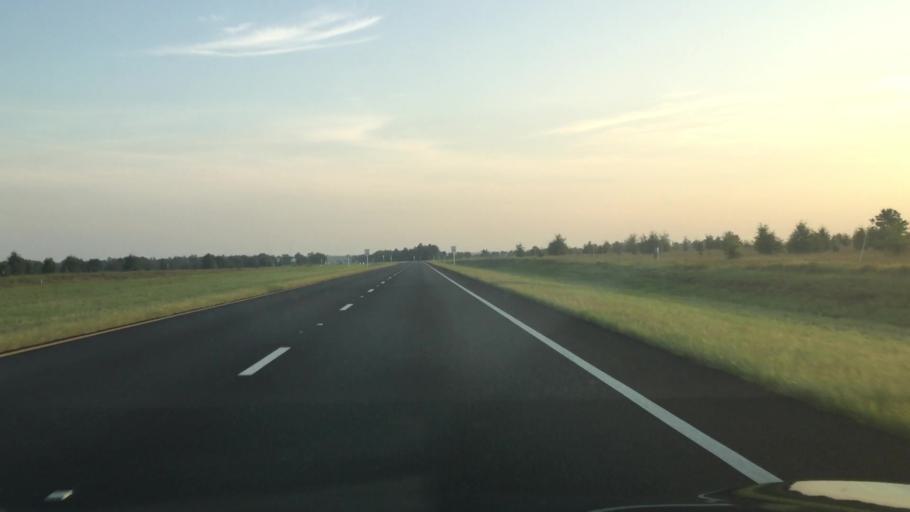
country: US
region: Florida
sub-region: Walton County
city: Freeport
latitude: 30.5479
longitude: -86.1065
